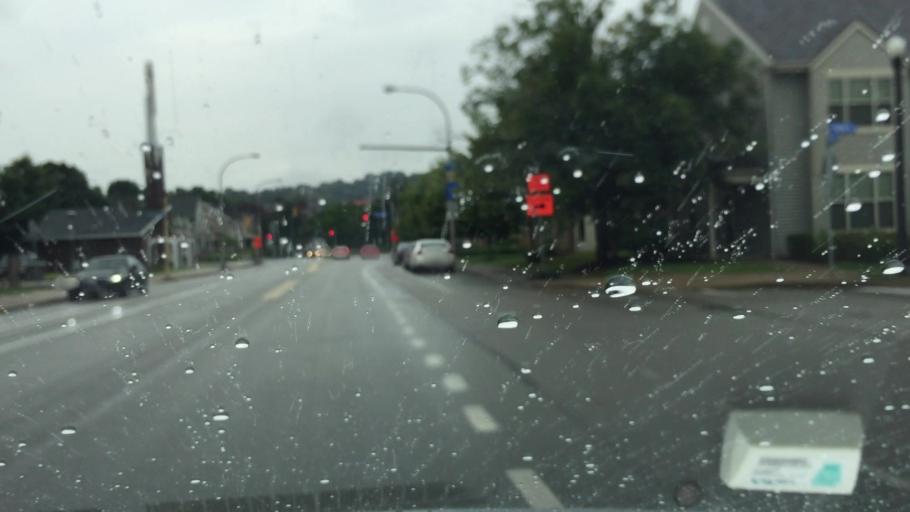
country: US
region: Pennsylvania
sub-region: Allegheny County
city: Bloomfield
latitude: 40.4641
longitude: -79.9205
